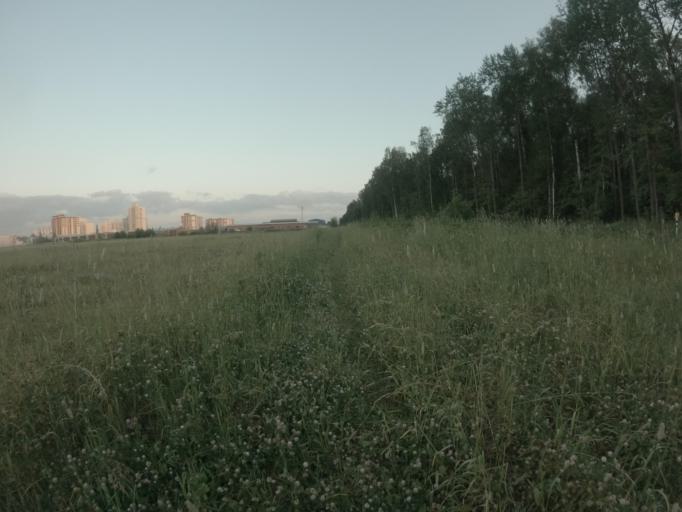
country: RU
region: Leningrad
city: Yanino Vtoroye
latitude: 59.9546
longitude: 30.5527
